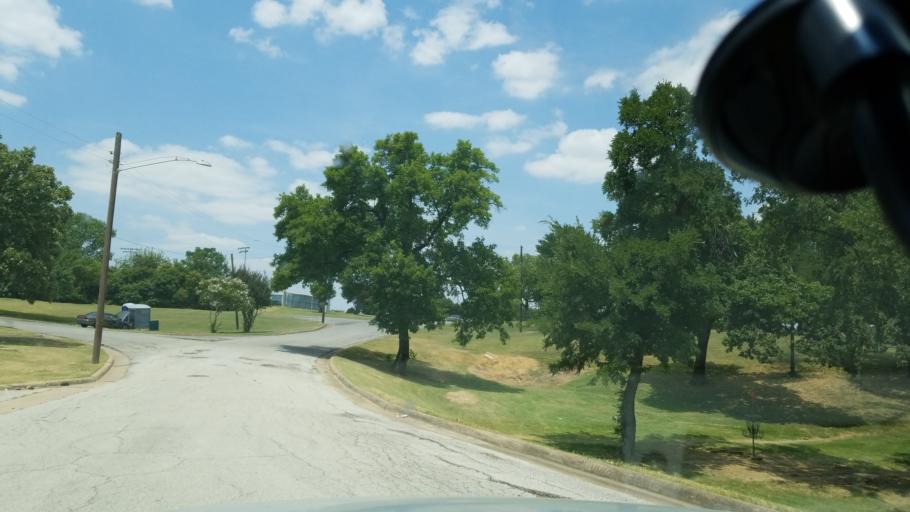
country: US
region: Texas
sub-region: Dallas County
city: Grand Prairie
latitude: 32.7527
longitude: -96.9958
